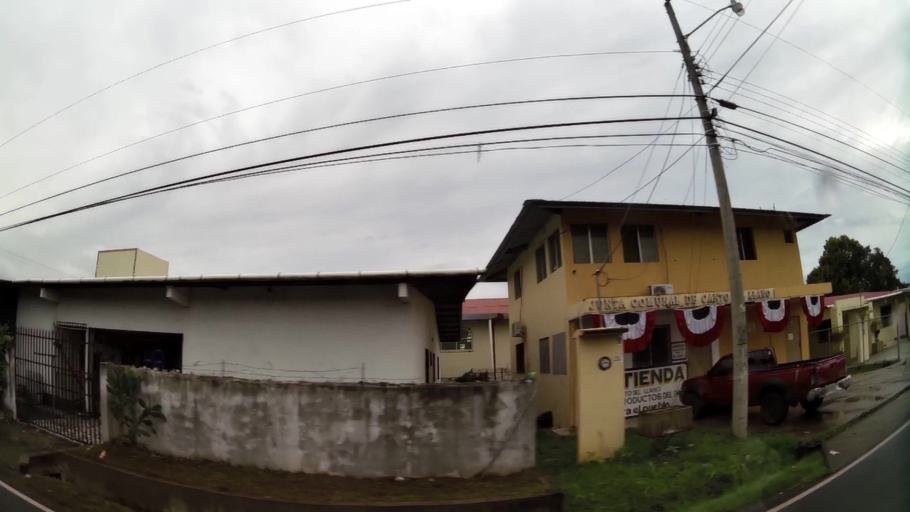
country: PA
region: Veraguas
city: Santiago de Veraguas
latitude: 8.1199
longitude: -80.9664
